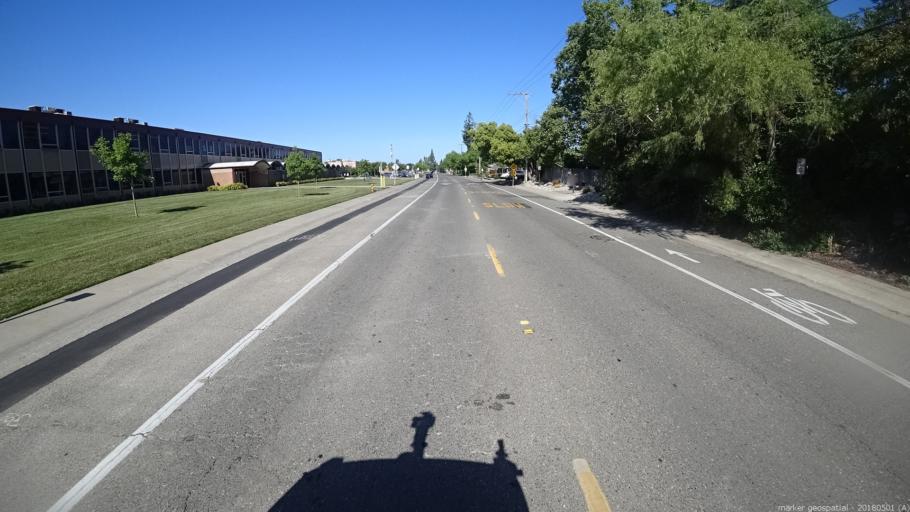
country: US
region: California
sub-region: Sacramento County
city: Arden-Arcade
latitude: 38.6341
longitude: -121.3694
